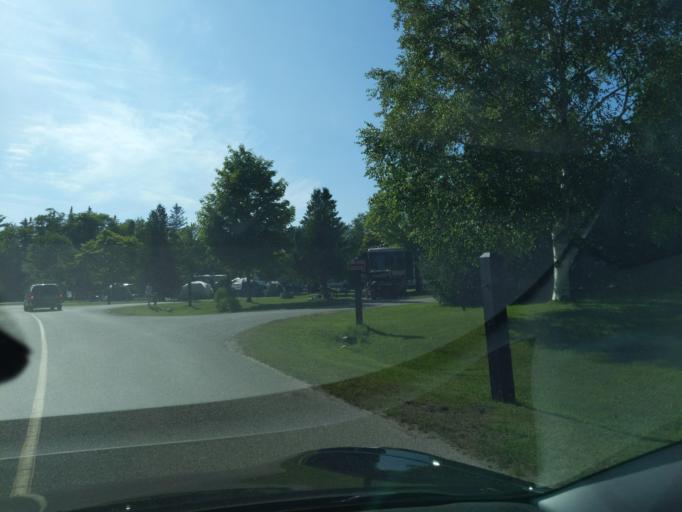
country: US
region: Michigan
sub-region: Mackinac County
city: Saint Ignace
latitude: 45.8534
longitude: -84.7208
